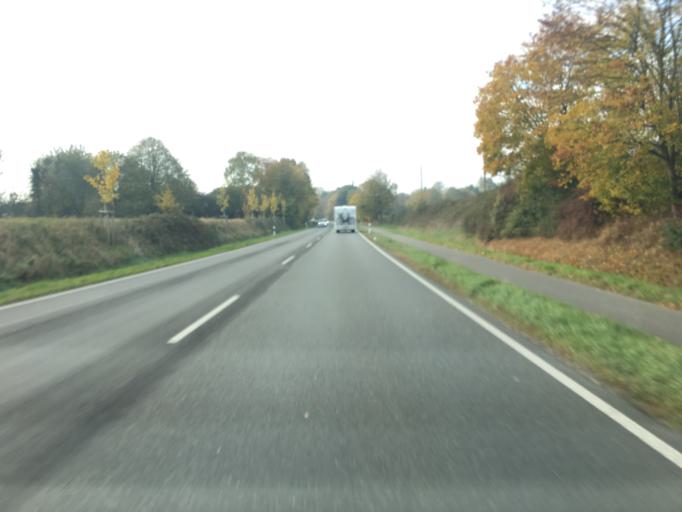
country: DE
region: North Rhine-Westphalia
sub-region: Regierungsbezirk Dusseldorf
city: Sonsbeck
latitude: 51.6197
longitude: 6.3845
